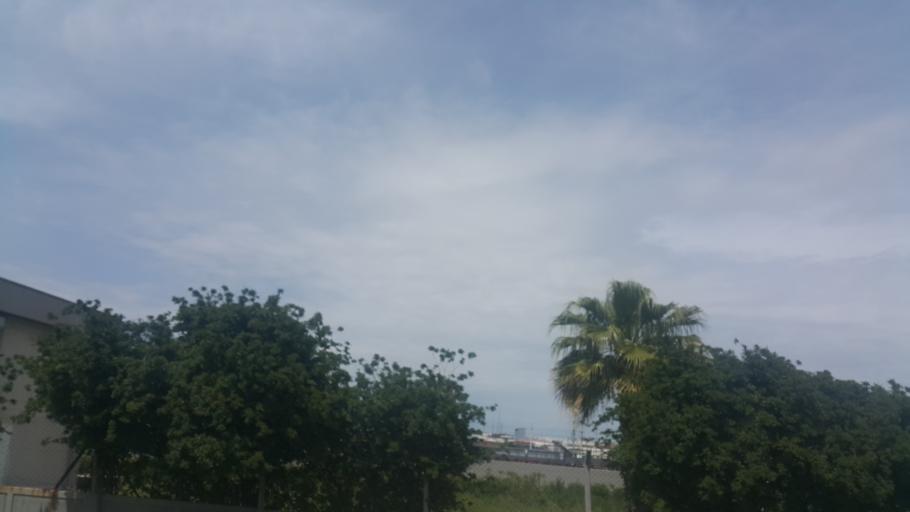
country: TR
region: Adana
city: Yakapinar
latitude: 36.9658
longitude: 35.6063
